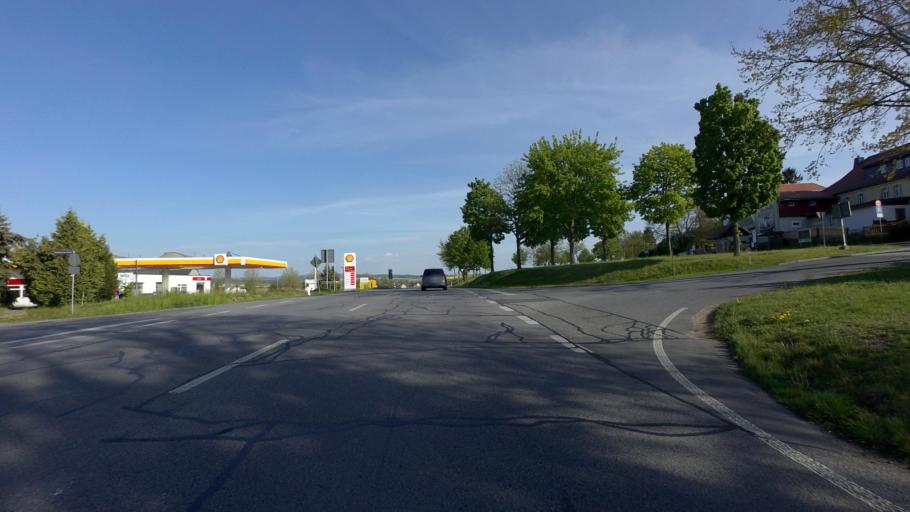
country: DE
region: Saxony
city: Stolpen
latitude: 51.0512
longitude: 14.0869
